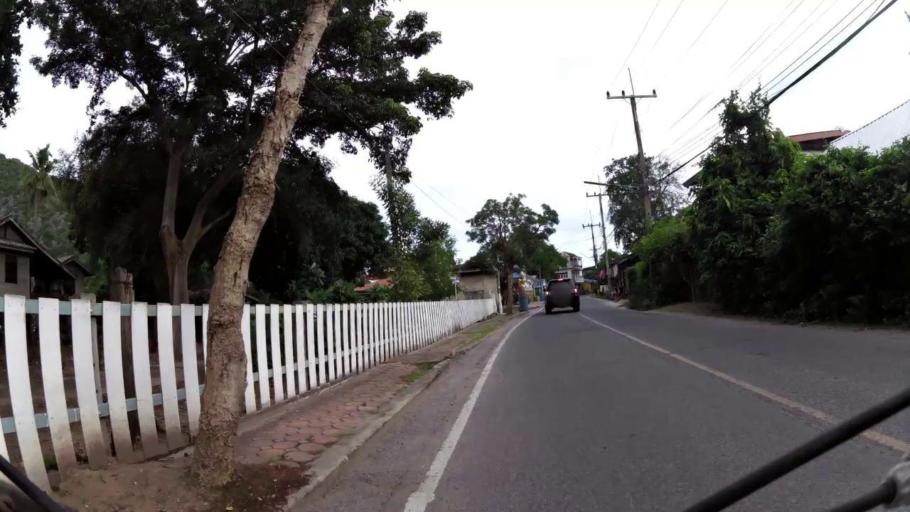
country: TH
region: Prachuap Khiri Khan
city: Prachuap Khiri Khan
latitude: 11.7486
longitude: 99.7901
